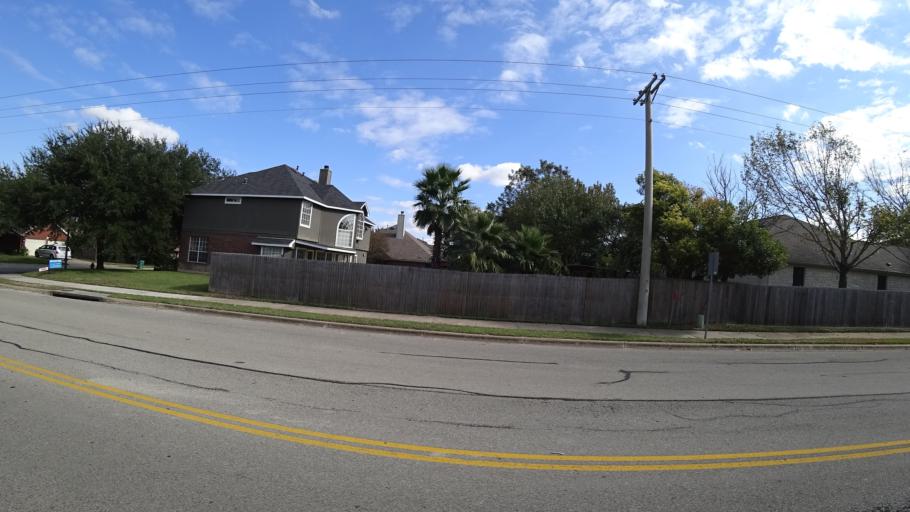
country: US
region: Texas
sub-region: Travis County
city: Pflugerville
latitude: 30.4344
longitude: -97.6319
